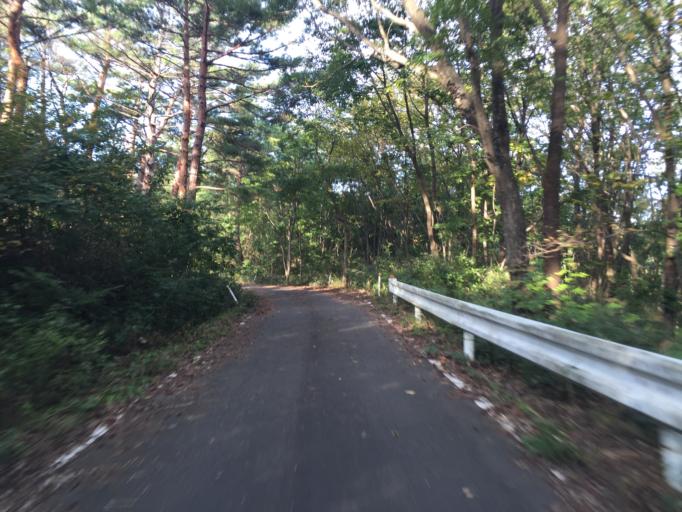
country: JP
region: Fukushima
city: Yanagawamachi-saiwaicho
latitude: 37.8967
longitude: 140.5441
